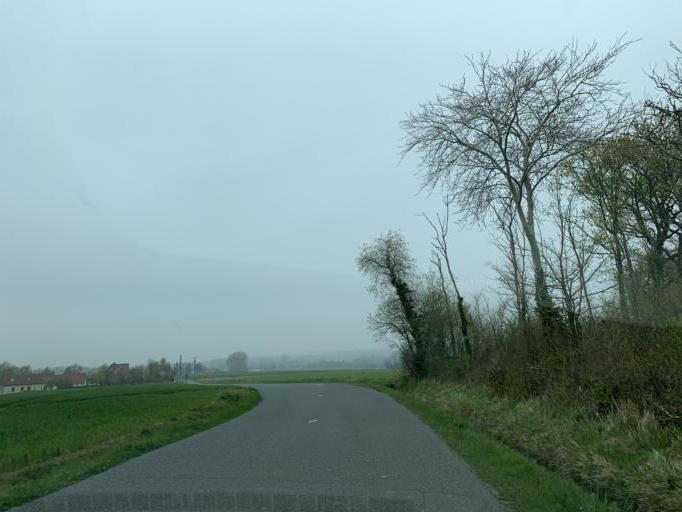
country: FR
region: Nord-Pas-de-Calais
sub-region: Departement du Pas-de-Calais
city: Rety
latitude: 50.7723
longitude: 1.7514
